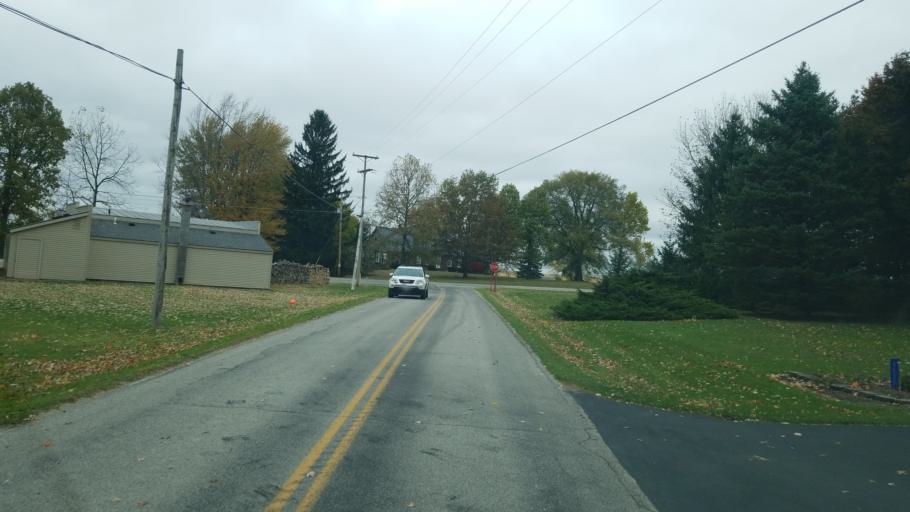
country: US
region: Ohio
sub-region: Crawford County
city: Bucyrus
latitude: 40.8723
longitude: -82.8731
